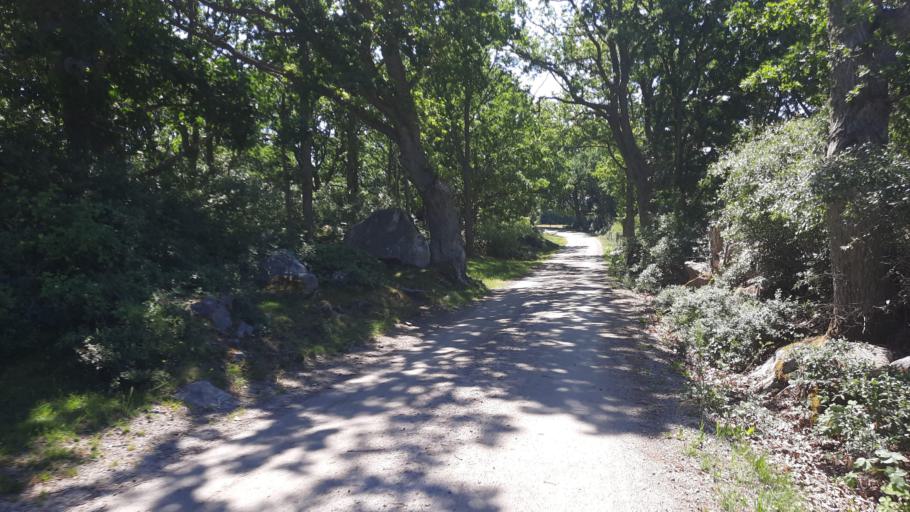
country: SE
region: Blekinge
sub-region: Karlskrona Kommun
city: Jaemjoe
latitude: 56.1531
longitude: 15.7528
